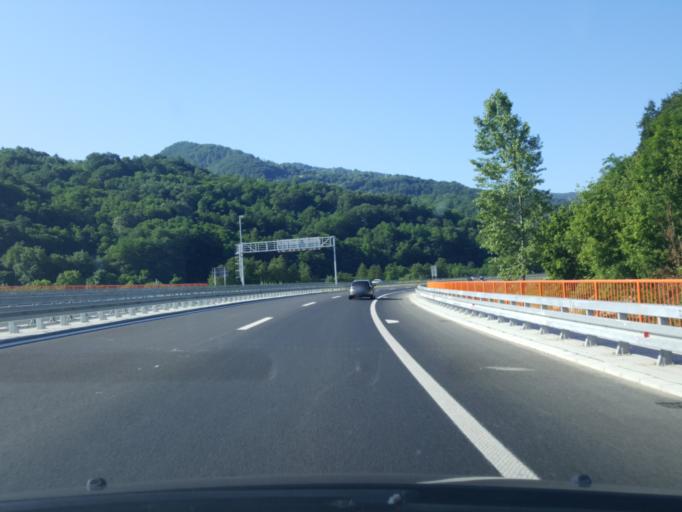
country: RS
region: Central Serbia
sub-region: Pcinjski Okrug
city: Vladicin Han
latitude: 42.8281
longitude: 22.1292
